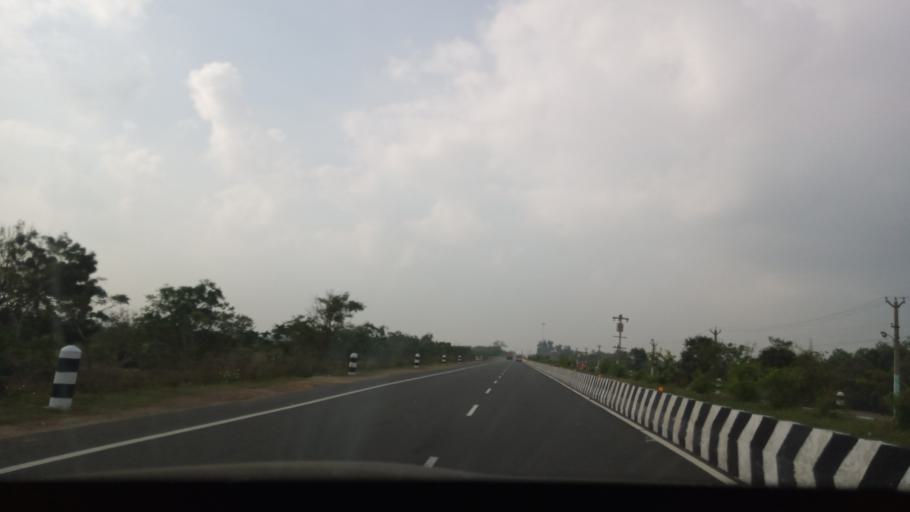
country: IN
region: Tamil Nadu
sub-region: Kancheepuram
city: Injambakkam
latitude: 12.7682
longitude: 80.2473
